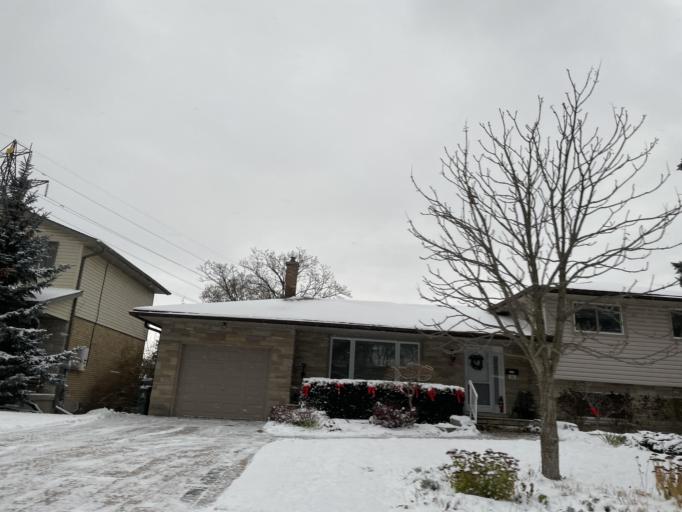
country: CA
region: Ontario
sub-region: Wellington County
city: Guelph
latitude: 43.5272
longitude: -80.2475
